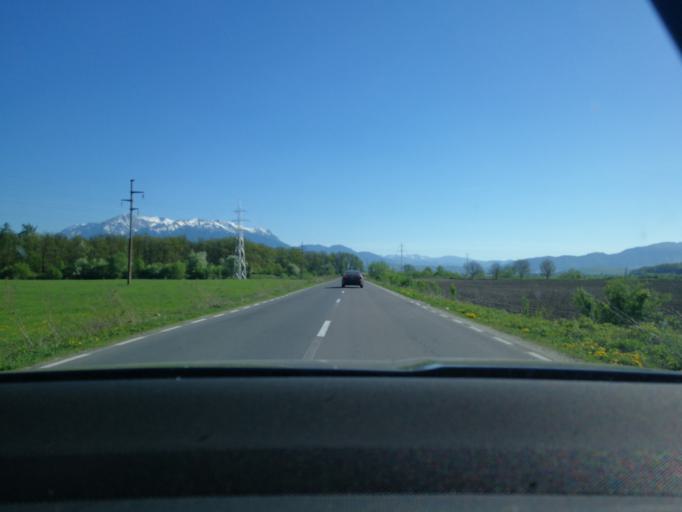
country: RO
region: Brasov
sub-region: Oras Rasnov
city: Rasnov
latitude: 45.5988
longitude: 25.4195
